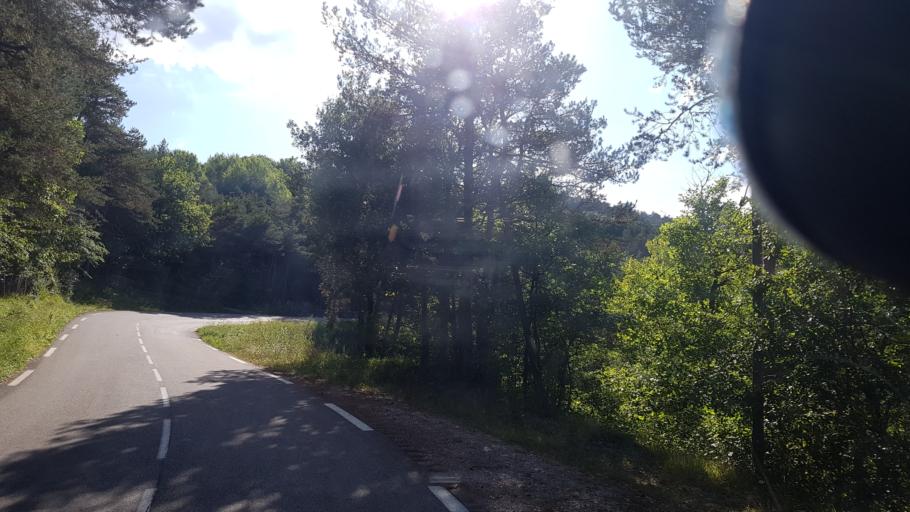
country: FR
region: Rhone-Alpes
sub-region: Departement de l'Isere
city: Mens
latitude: 44.8278
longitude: 5.6395
